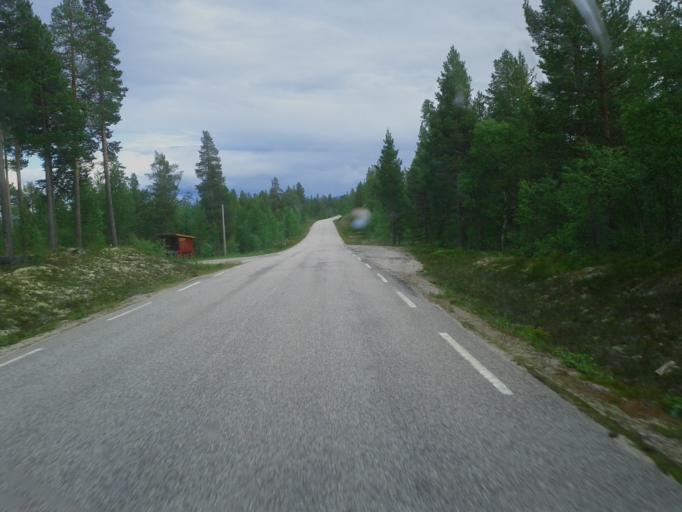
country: NO
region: Hedmark
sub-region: Engerdal
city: Engerdal
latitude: 62.0425
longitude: 11.6953
